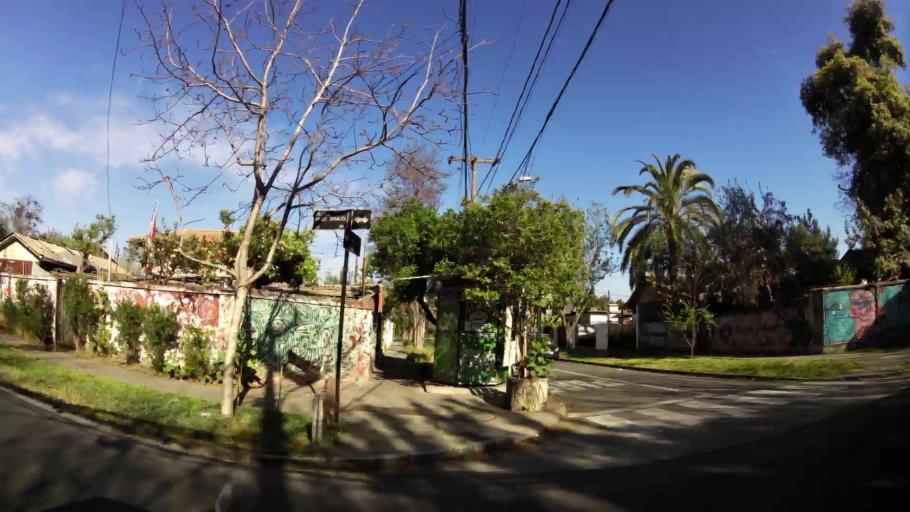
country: CL
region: Santiago Metropolitan
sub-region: Provincia de Santiago
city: Villa Presidente Frei, Nunoa, Santiago, Chile
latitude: -33.4492
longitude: -70.5514
